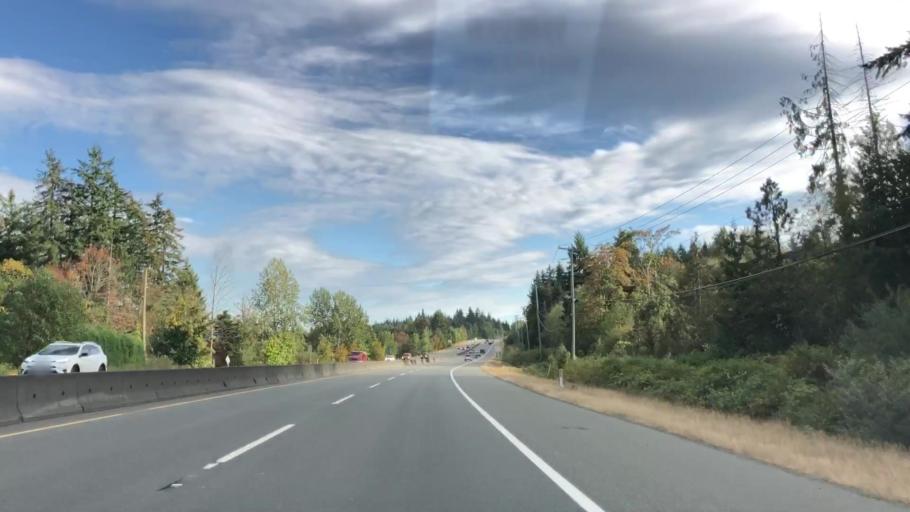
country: CA
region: British Columbia
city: North Saanich
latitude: 48.6383
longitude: -123.5513
